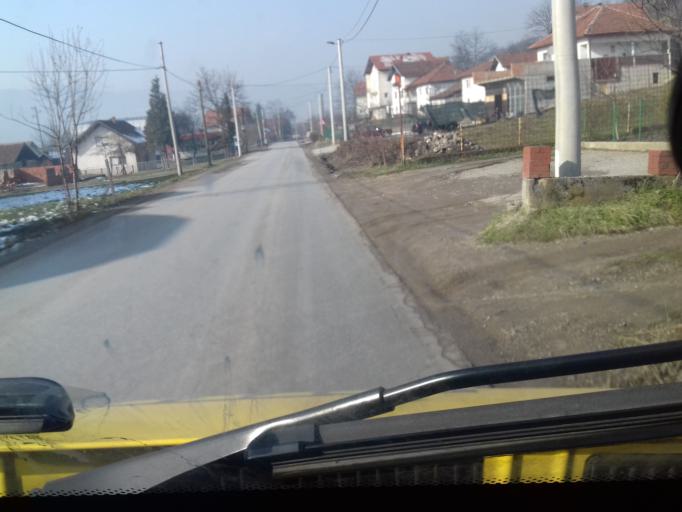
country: BA
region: Federation of Bosnia and Herzegovina
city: Ilijas
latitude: 43.9419
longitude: 18.2757
